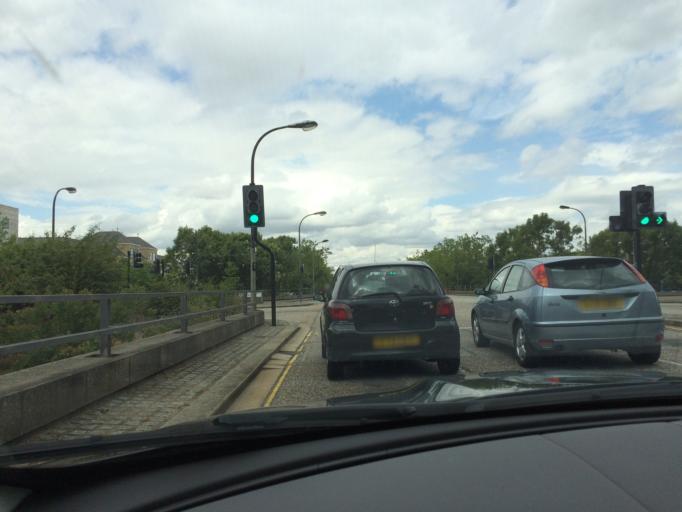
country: GB
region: England
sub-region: Milton Keynes
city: Milton Keynes
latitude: 52.0380
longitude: -0.7646
